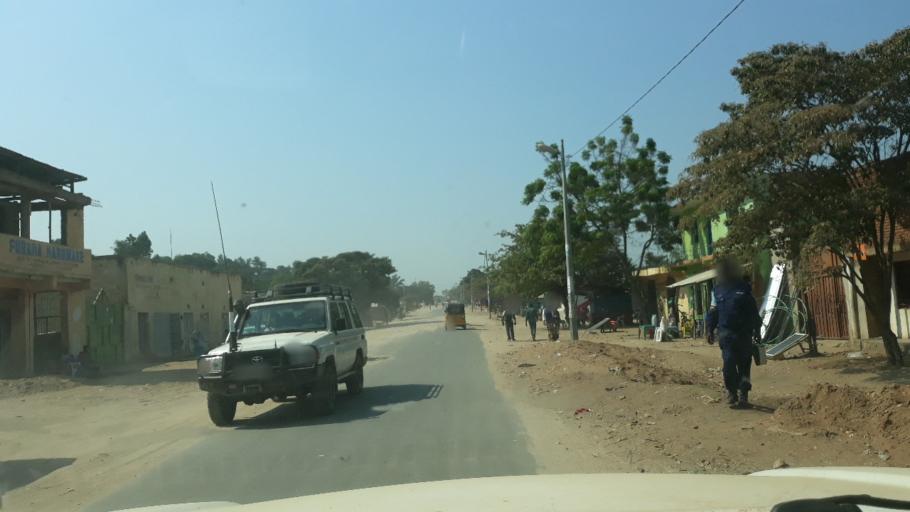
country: CD
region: South Kivu
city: Uvira
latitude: -3.3586
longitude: 29.1526
